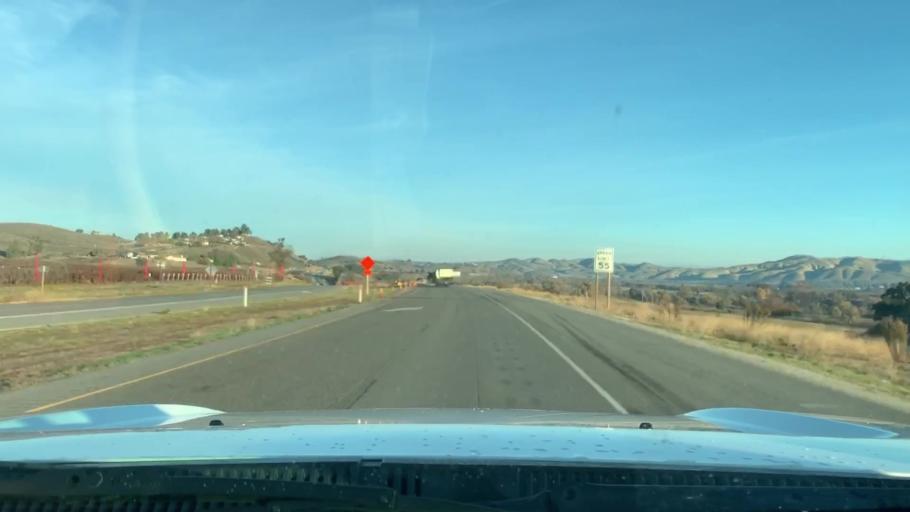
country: US
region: California
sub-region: San Luis Obispo County
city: San Miguel
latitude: 35.7142
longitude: -120.6942
